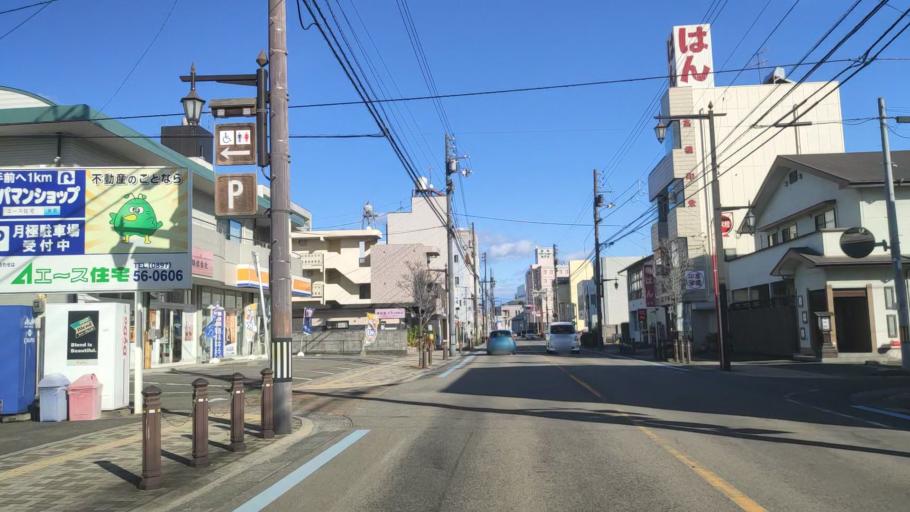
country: JP
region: Ehime
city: Saijo
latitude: 33.9127
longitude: 133.1853
